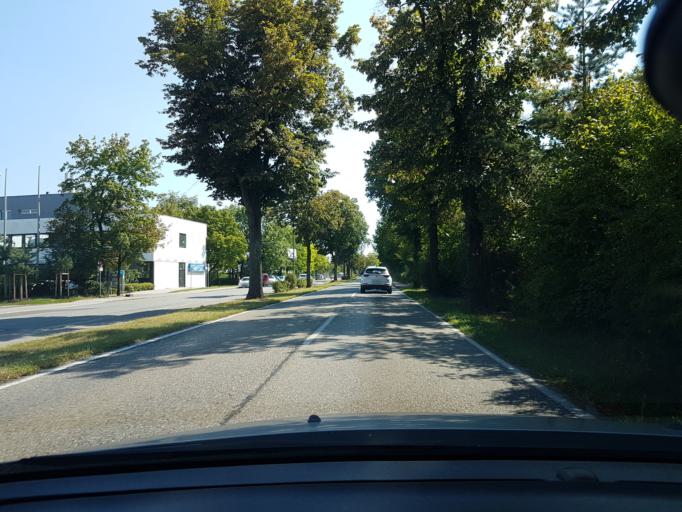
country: DE
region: Bavaria
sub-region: Upper Bavaria
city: Oberschleissheim
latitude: 48.2624
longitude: 11.5571
